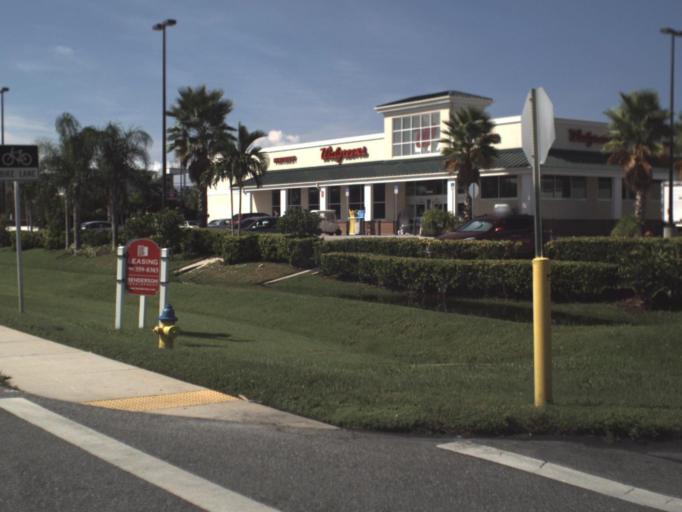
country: US
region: Florida
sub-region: Manatee County
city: Holmes Beach
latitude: 27.4923
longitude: -82.7074
